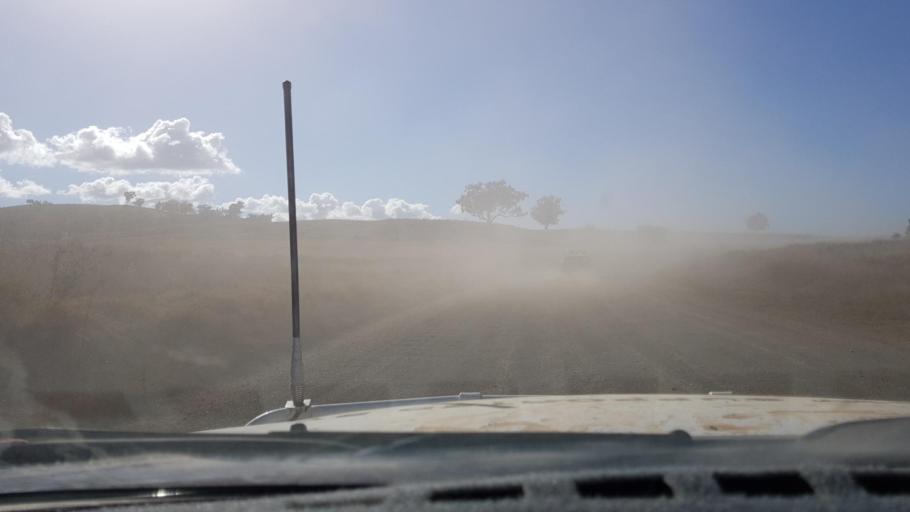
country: AU
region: New South Wales
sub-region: Narrabri
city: Blair Athol
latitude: -30.6724
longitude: 150.4009
